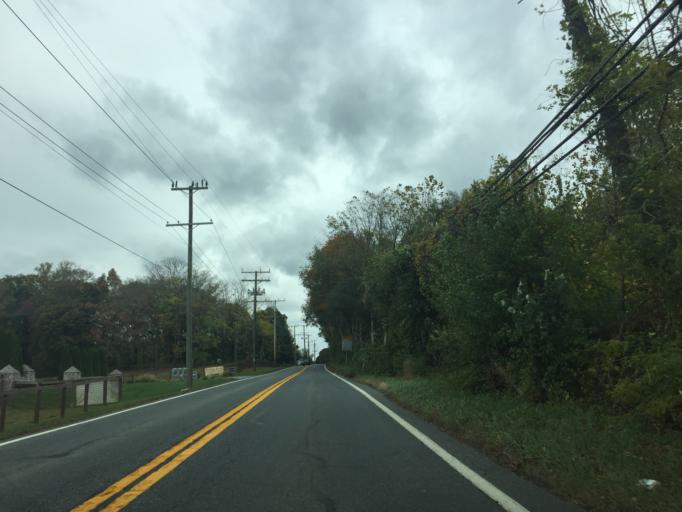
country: US
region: Maryland
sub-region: Harford County
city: Riverside
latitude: 39.5325
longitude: -76.2617
